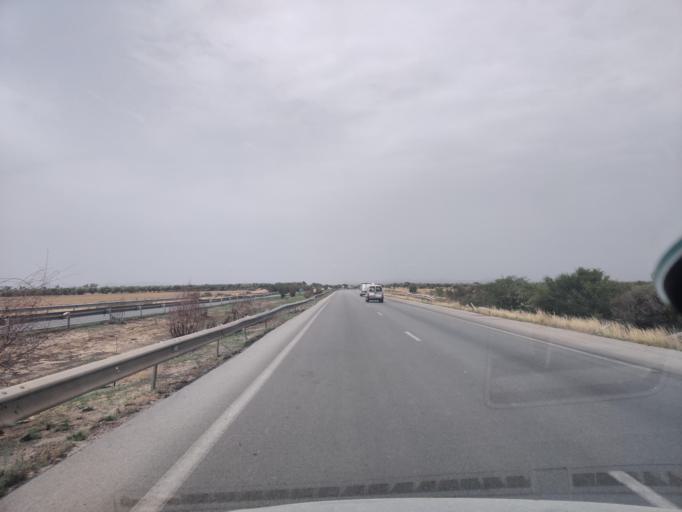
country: TN
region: Susah
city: Harqalah
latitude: 36.0506
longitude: 10.4132
